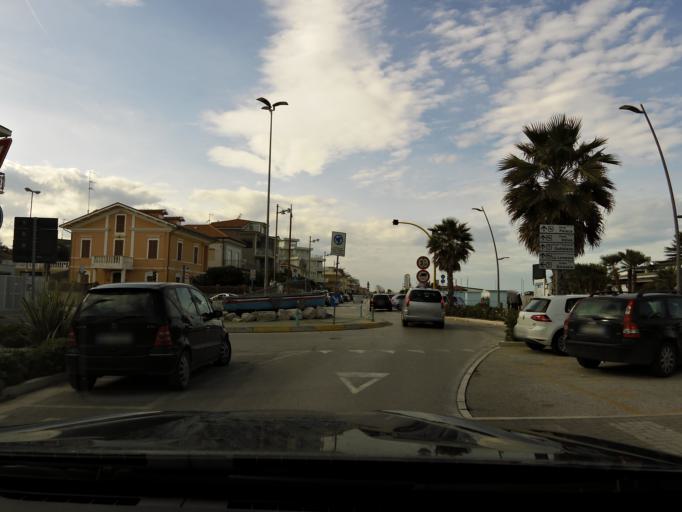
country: IT
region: The Marches
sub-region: Provincia di Macerata
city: Civitanova Marche
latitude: 43.3163
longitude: 13.7234
